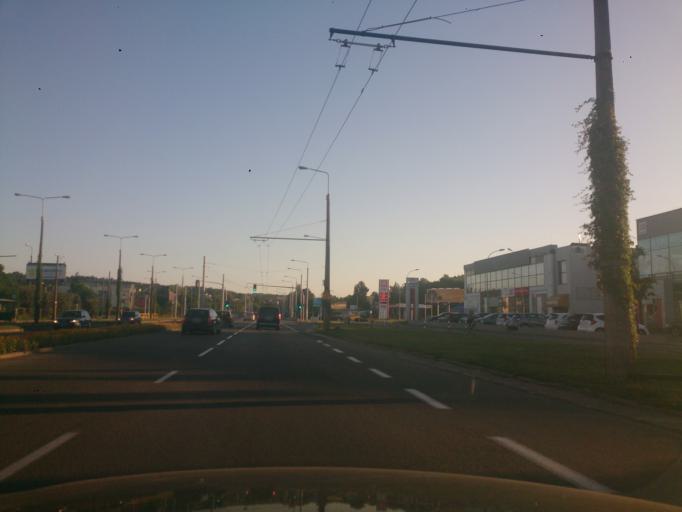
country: PL
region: Pomeranian Voivodeship
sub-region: Gdynia
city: Wielki Kack
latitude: 54.4742
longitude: 18.5149
